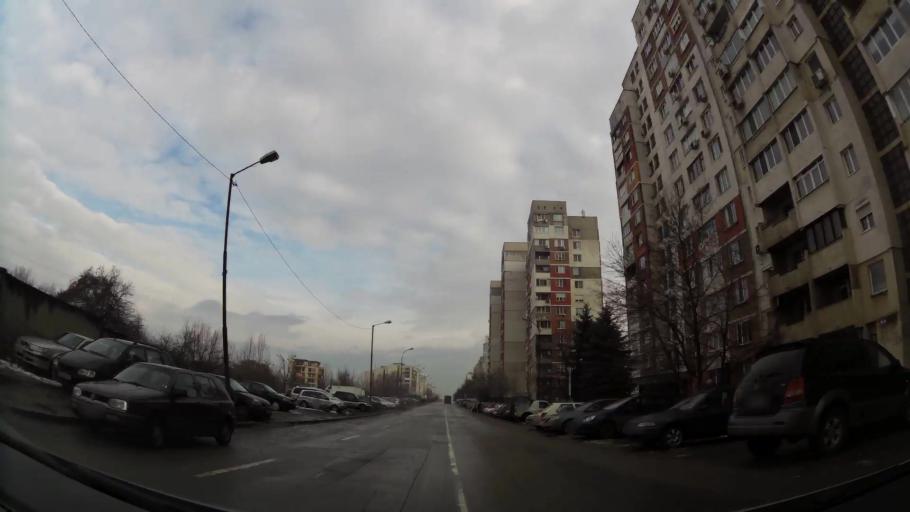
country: BG
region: Sofiya
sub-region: Obshtina Bozhurishte
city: Bozhurishte
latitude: 42.7170
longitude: 23.2375
